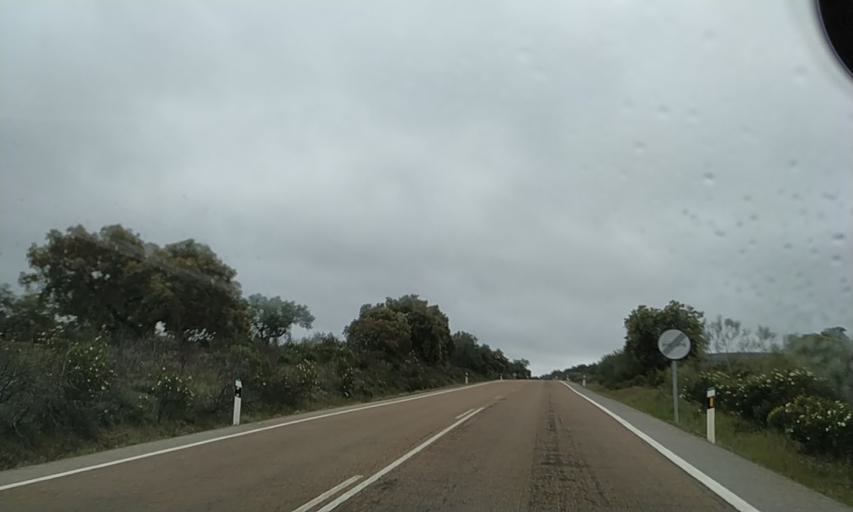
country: ES
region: Extremadura
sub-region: Provincia de Badajoz
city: Puebla de Obando
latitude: 39.2863
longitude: -6.5220
